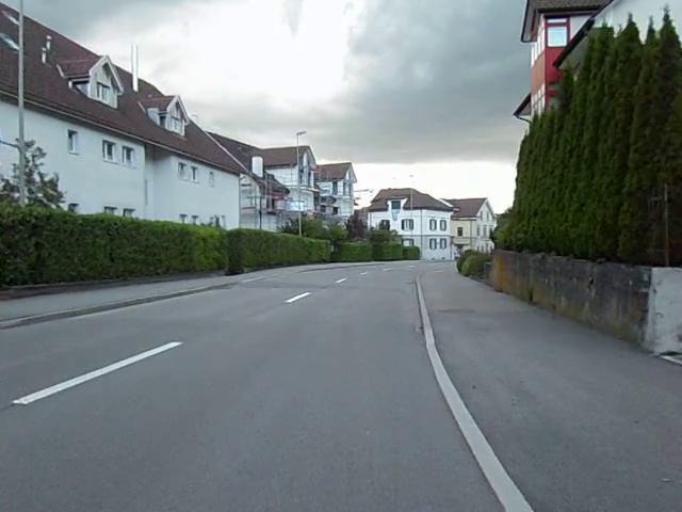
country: CH
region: Zurich
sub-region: Bezirk Hinwil
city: Rueti
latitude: 47.2569
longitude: 8.8541
